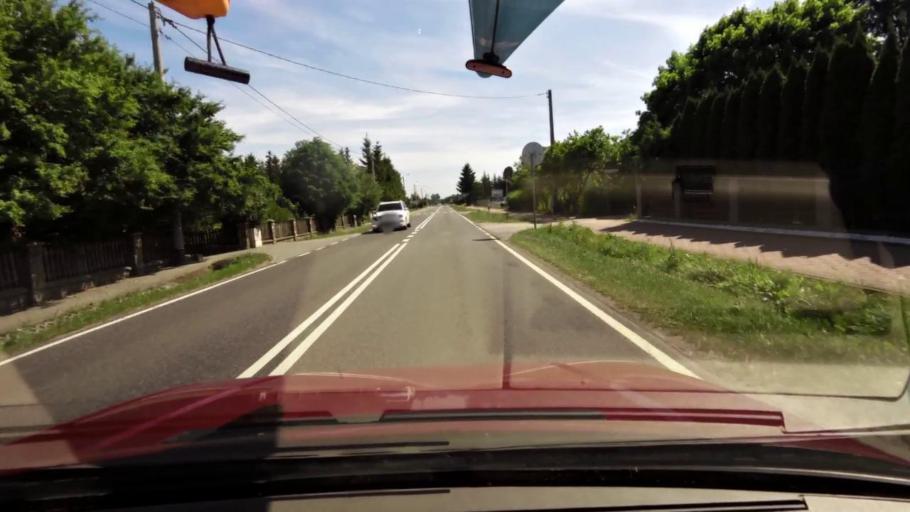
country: PL
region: Pomeranian Voivodeship
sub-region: Powiat slupski
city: Kobylnica
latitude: 54.4204
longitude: 17.0074
